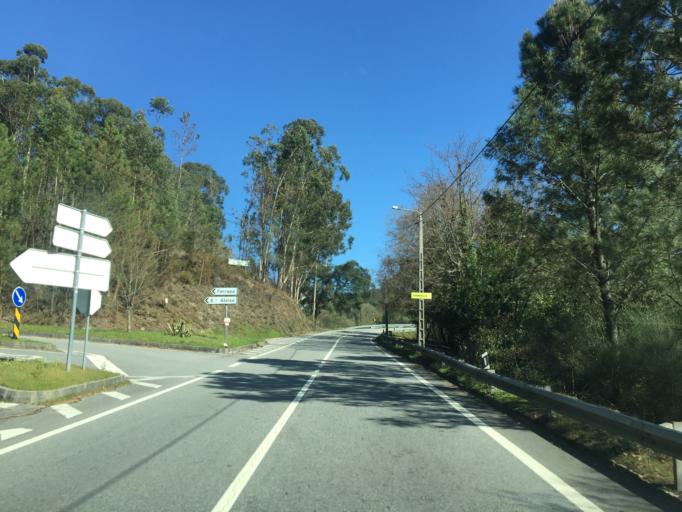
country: PT
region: Aveiro
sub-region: Vale de Cambra
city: Macieira de Cambra
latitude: 40.8895
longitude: -8.3591
